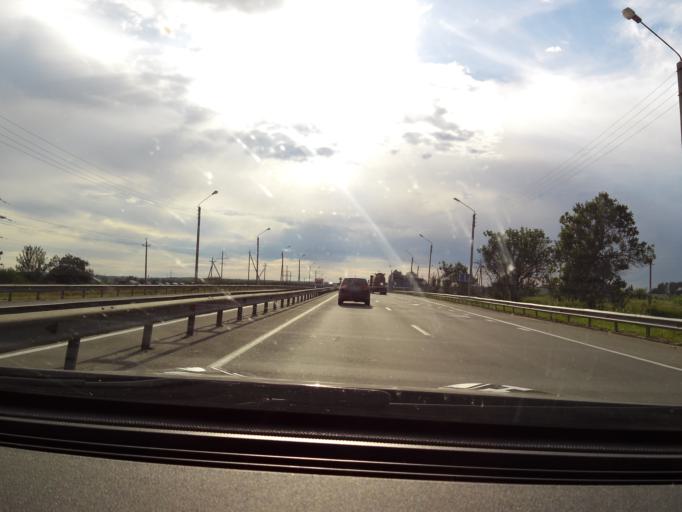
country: RU
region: Vladimir
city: Novovyazniki
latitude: 56.2188
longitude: 42.1978
